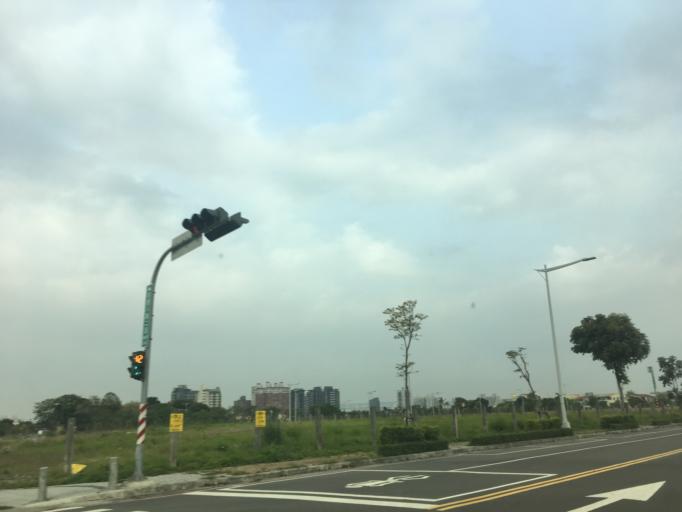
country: TW
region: Taiwan
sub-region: Taichung City
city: Taichung
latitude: 24.1912
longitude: 120.6749
